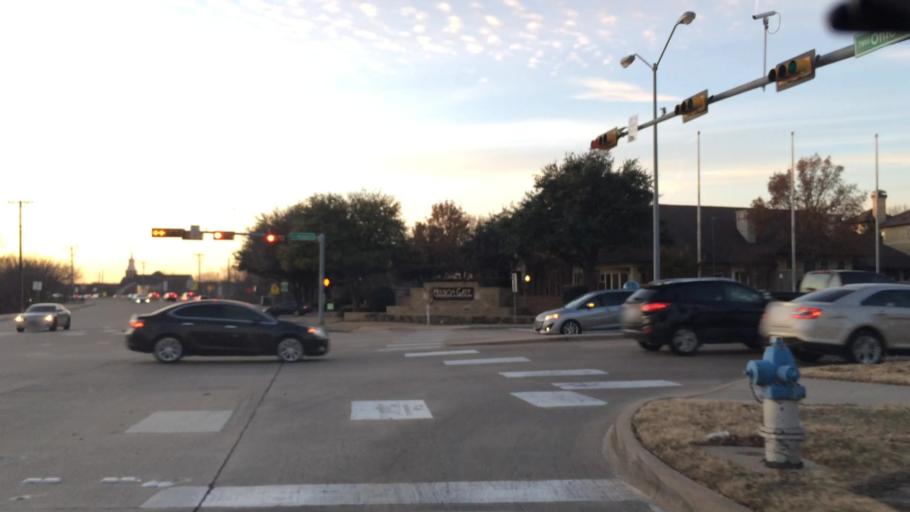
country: US
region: Texas
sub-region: Collin County
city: Frisco
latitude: 33.0877
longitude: -96.7970
